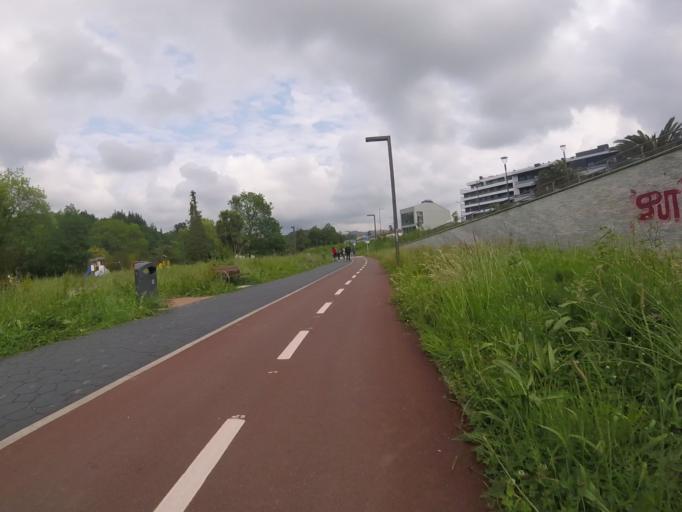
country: ES
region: Basque Country
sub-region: Provincia de Guipuzcoa
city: San Sebastian
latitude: 43.3053
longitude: -1.9583
